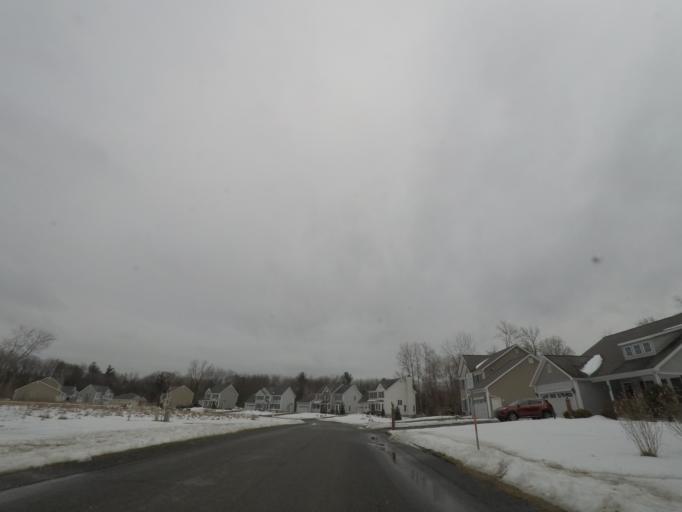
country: US
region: New York
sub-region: Schenectady County
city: Rotterdam
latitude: 42.7631
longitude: -73.9735
